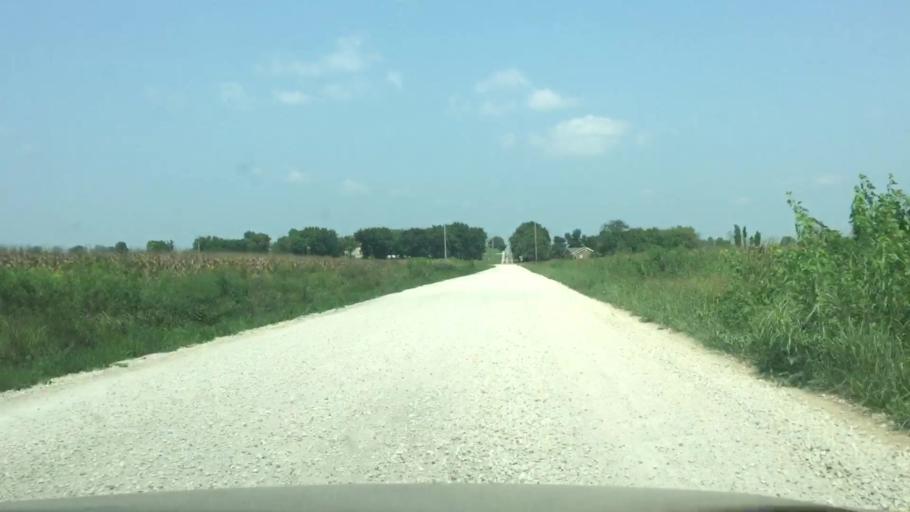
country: US
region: Kansas
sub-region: Allen County
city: Iola
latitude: 37.8757
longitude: -95.3911
